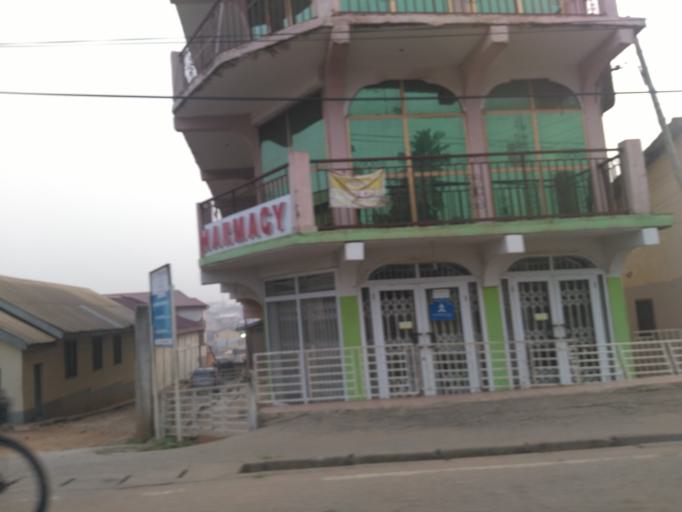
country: GH
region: Ashanti
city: Kumasi
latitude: 6.6859
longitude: -1.6175
